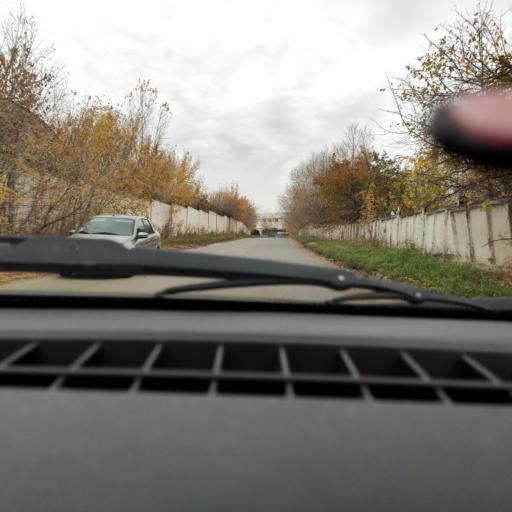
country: RU
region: Bashkortostan
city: Ufa
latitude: 54.8370
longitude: 56.0788
